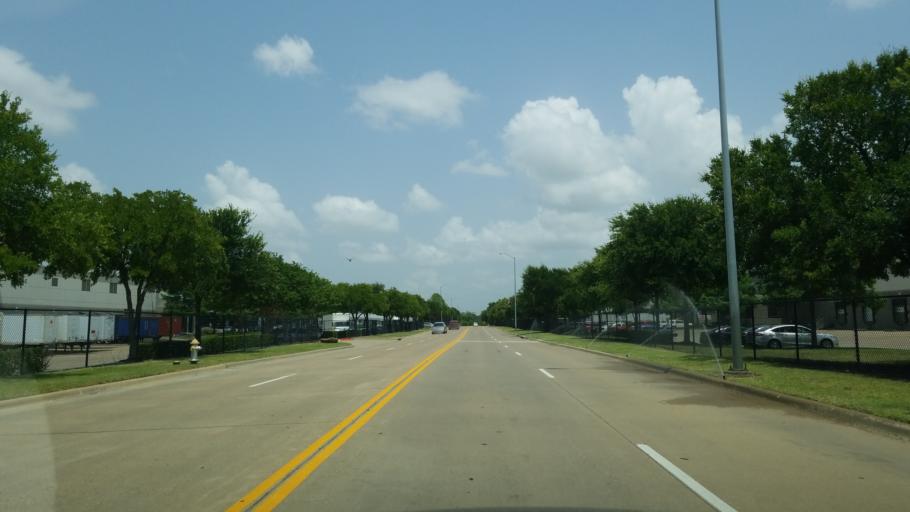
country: US
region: Texas
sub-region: Dallas County
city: Cockrell Hill
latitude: 32.7599
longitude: -96.8857
